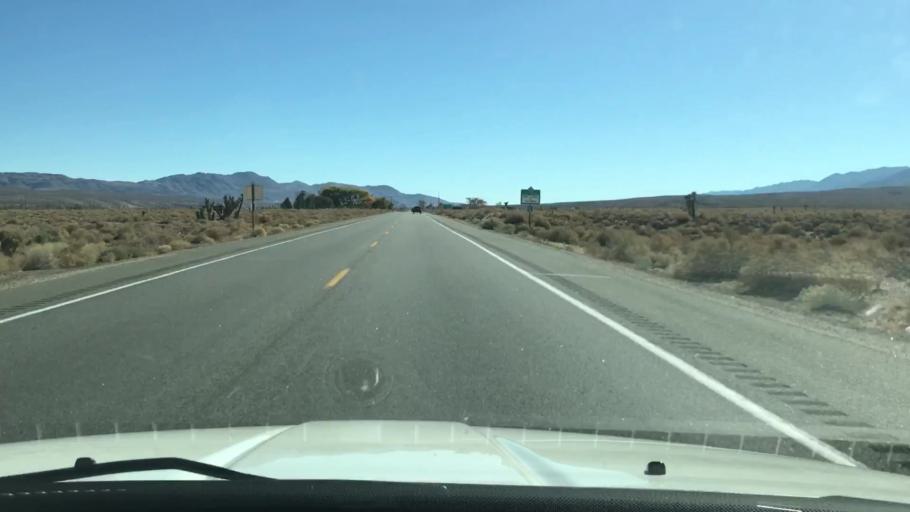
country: US
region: California
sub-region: Inyo County
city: Lone Pine
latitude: 36.2636
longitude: -117.9972
